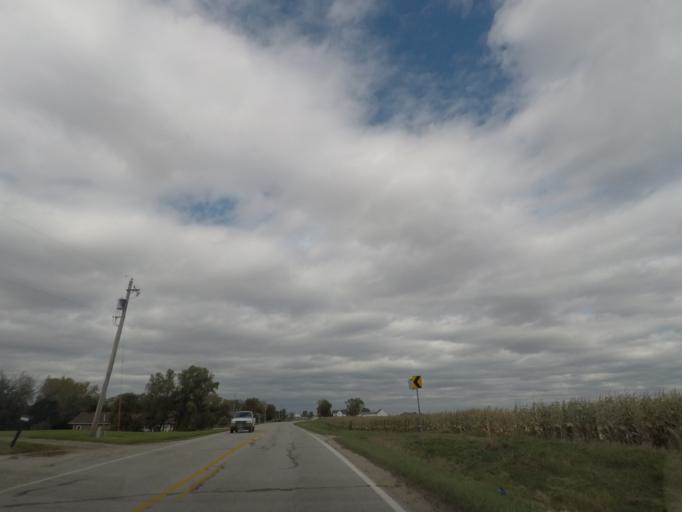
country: US
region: Iowa
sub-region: Story County
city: Huxley
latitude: 41.8390
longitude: -93.5313
